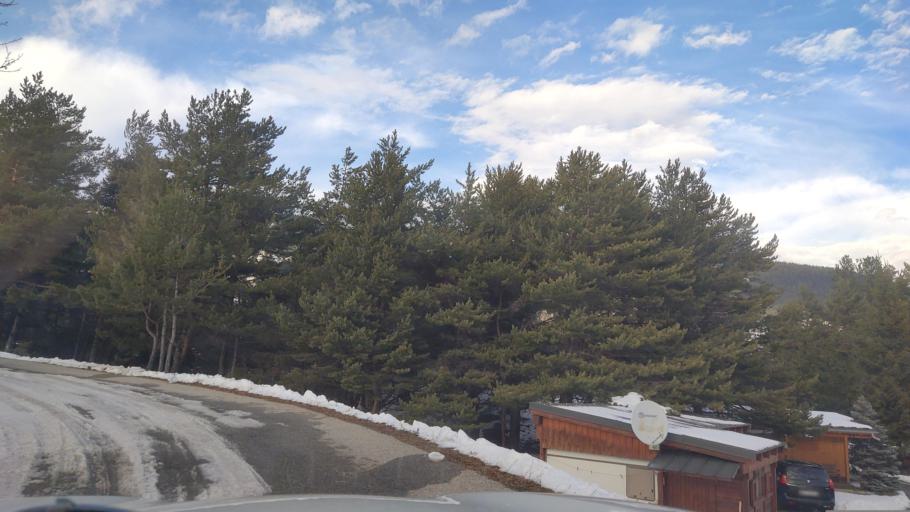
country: FR
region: Rhone-Alpes
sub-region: Departement de la Savoie
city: Modane
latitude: 45.2240
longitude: 6.7451
